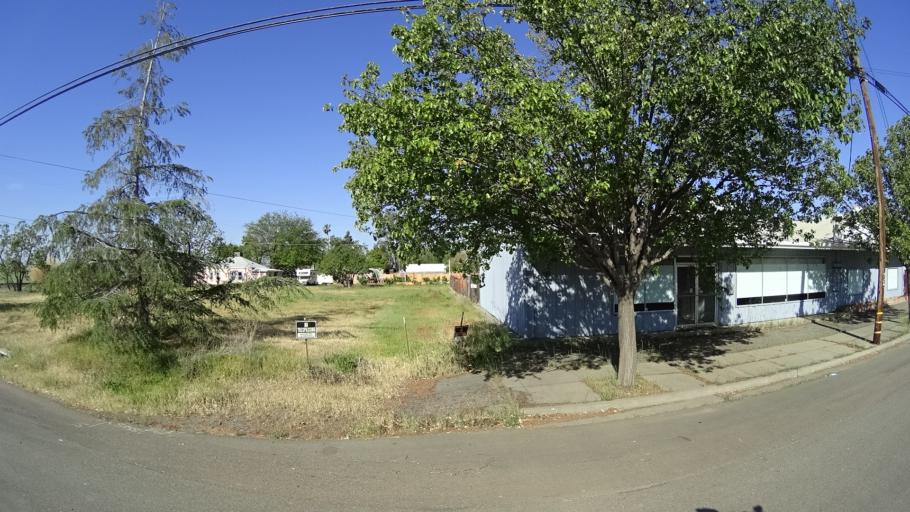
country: US
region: California
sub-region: Glenn County
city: Willows
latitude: 39.5101
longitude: -122.1939
